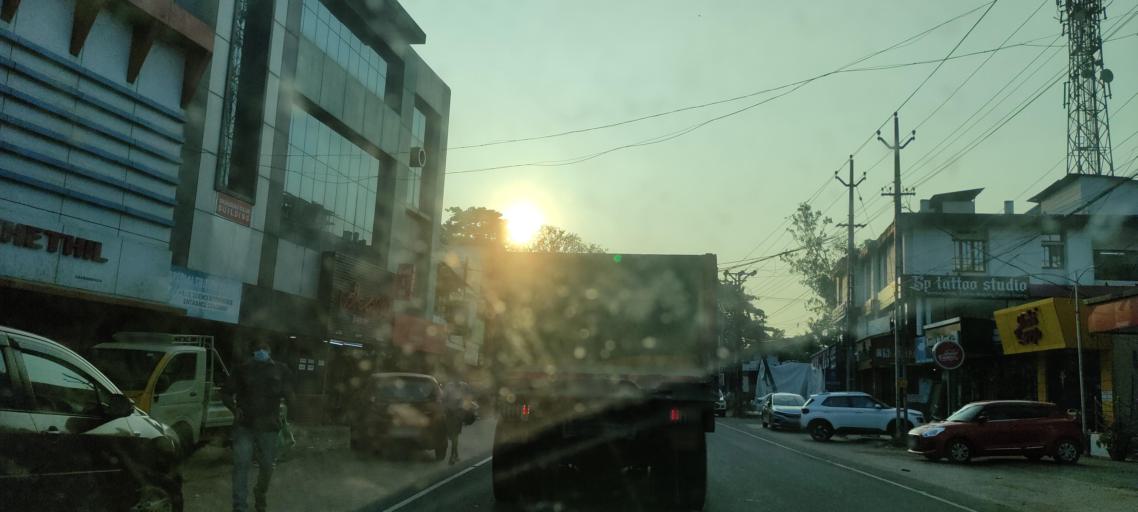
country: IN
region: Kerala
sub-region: Alappuzha
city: Kattanam
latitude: 9.1747
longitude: 76.6114
